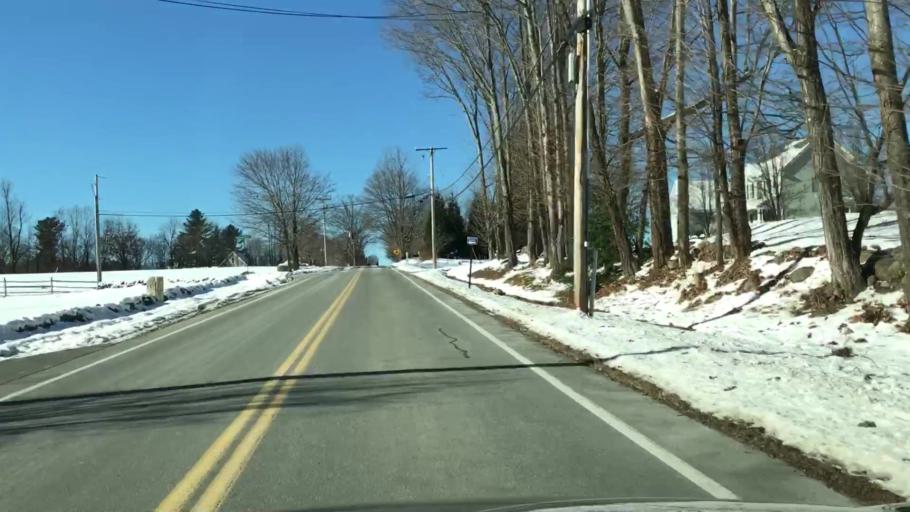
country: US
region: New Hampshire
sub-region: Hillsborough County
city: Bedford
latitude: 42.9247
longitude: -71.5711
